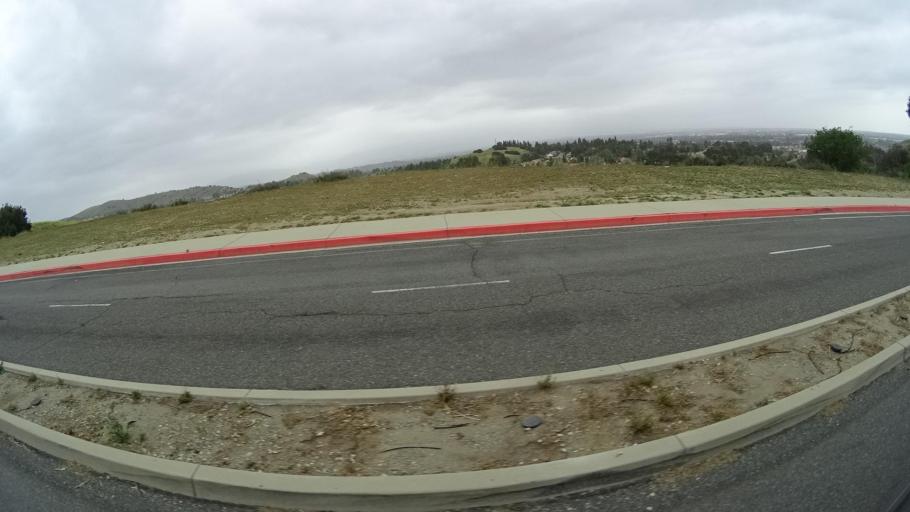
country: US
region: California
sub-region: San Bernardino County
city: Chino Hills
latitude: 34.0223
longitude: -117.7731
